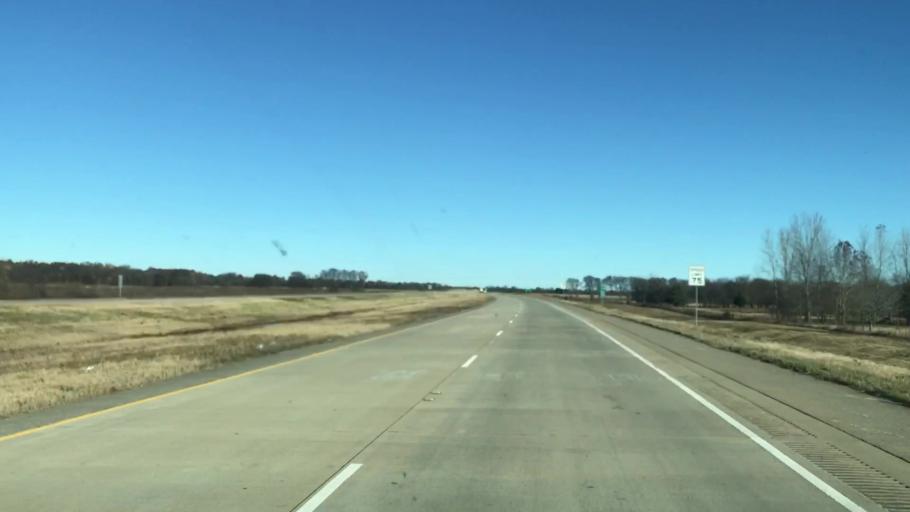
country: US
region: Louisiana
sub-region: Caddo Parish
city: Vivian
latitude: 32.8632
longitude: -93.8603
